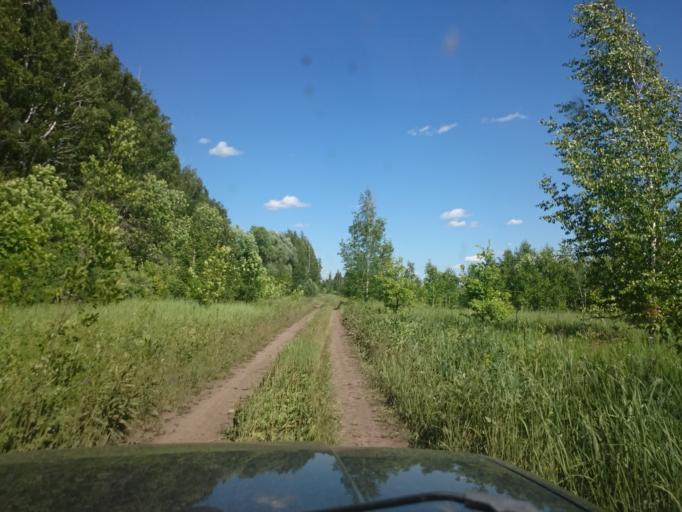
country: RU
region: Mordoviya
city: Kadoshkino
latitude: 54.0523
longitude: 44.4769
